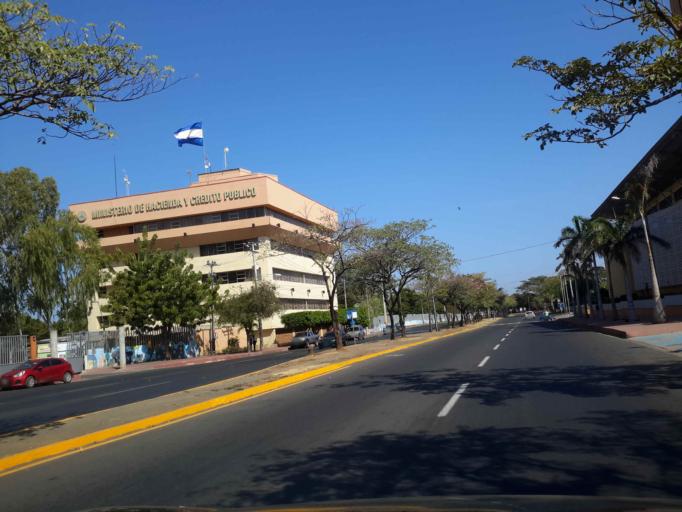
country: NI
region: Managua
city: Managua
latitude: 12.1509
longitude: -86.2739
